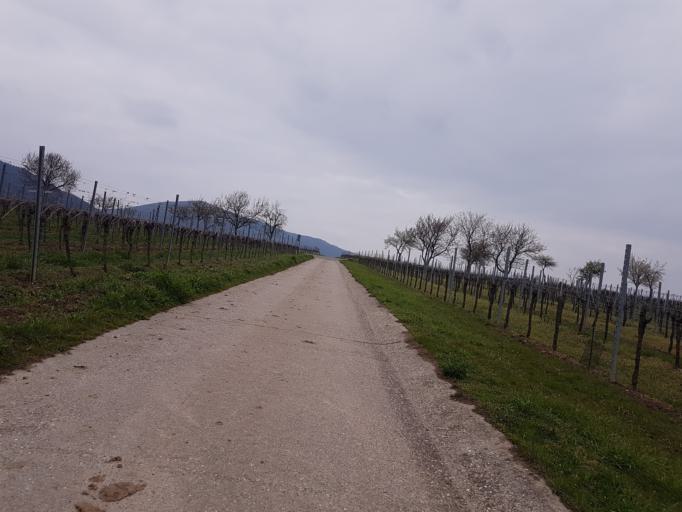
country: DE
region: Rheinland-Pfalz
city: Burrweiler
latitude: 49.2375
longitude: 8.0806
